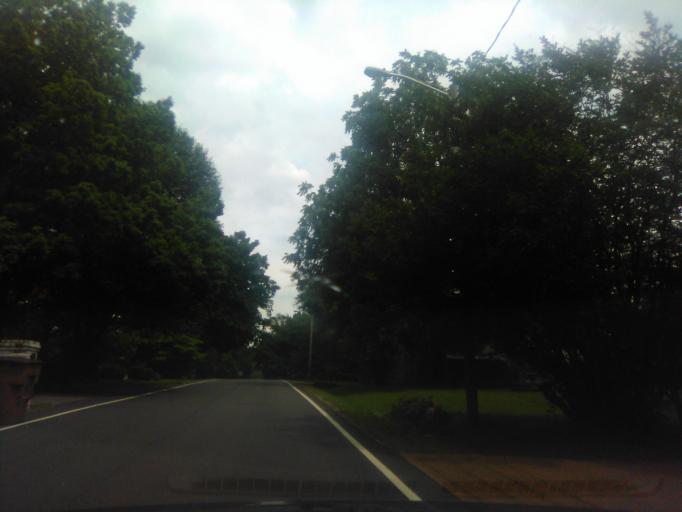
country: US
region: Tennessee
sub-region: Davidson County
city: Belle Meade
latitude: 36.0919
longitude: -86.8739
